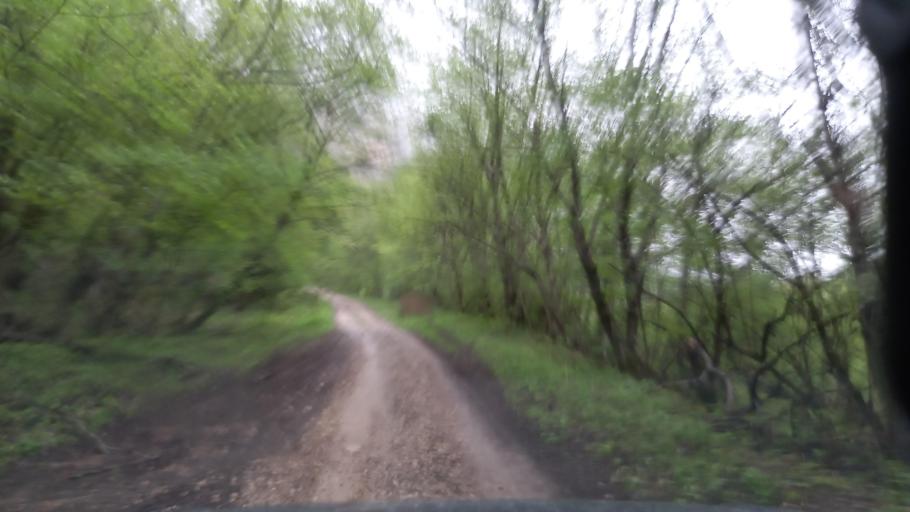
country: RU
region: Kabardino-Balkariya
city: Bylym
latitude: 43.5911
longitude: 42.9835
